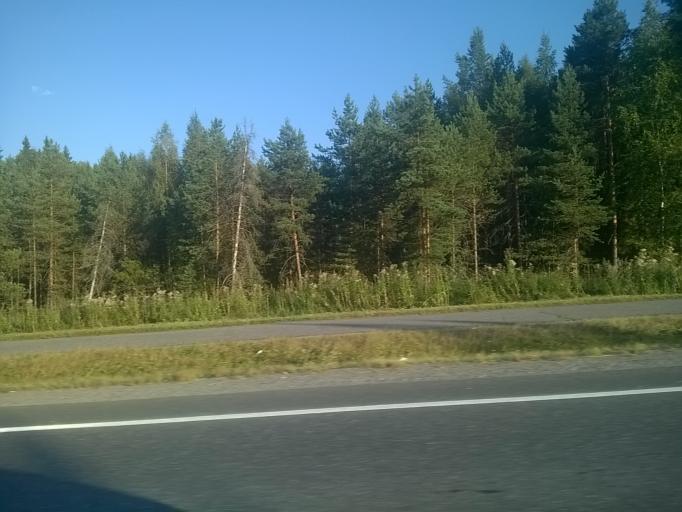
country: FI
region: Pirkanmaa
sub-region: Tampere
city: Tampere
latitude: 61.4334
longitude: 23.8359
